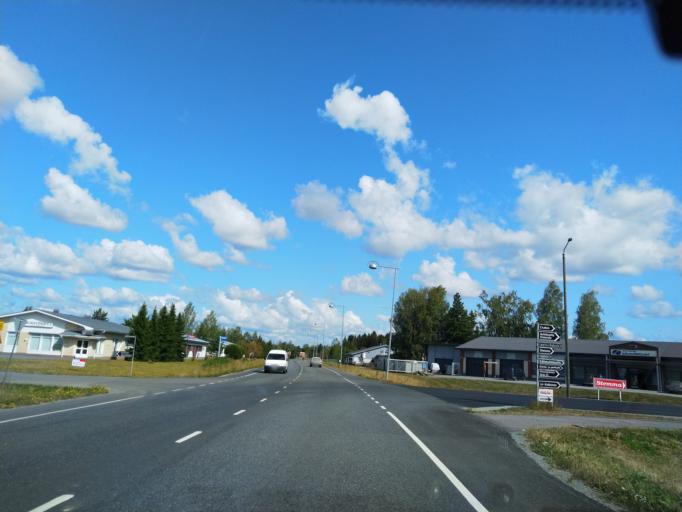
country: FI
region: Satakunta
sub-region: Pori
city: Huittinen
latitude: 61.1686
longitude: 22.7080
